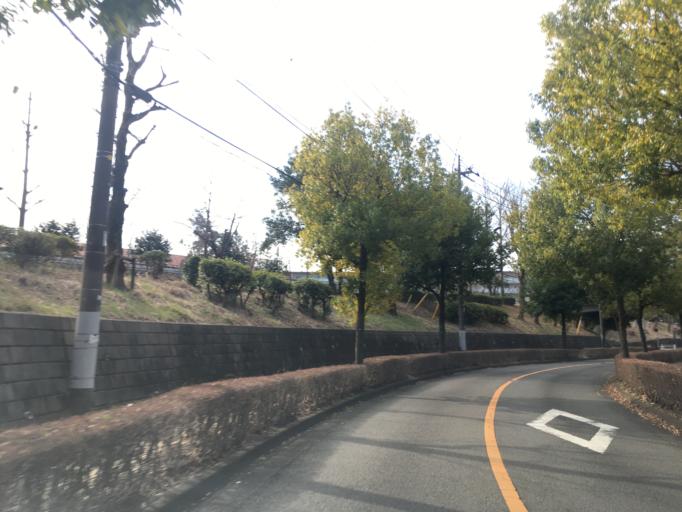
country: JP
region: Tokyo
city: Hino
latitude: 35.6138
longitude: 139.4355
